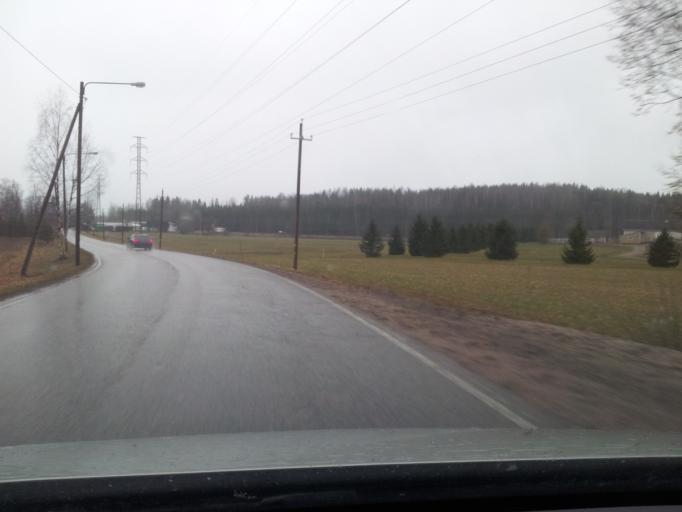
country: FI
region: Uusimaa
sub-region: Helsinki
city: Espoo
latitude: 60.1958
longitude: 24.5698
